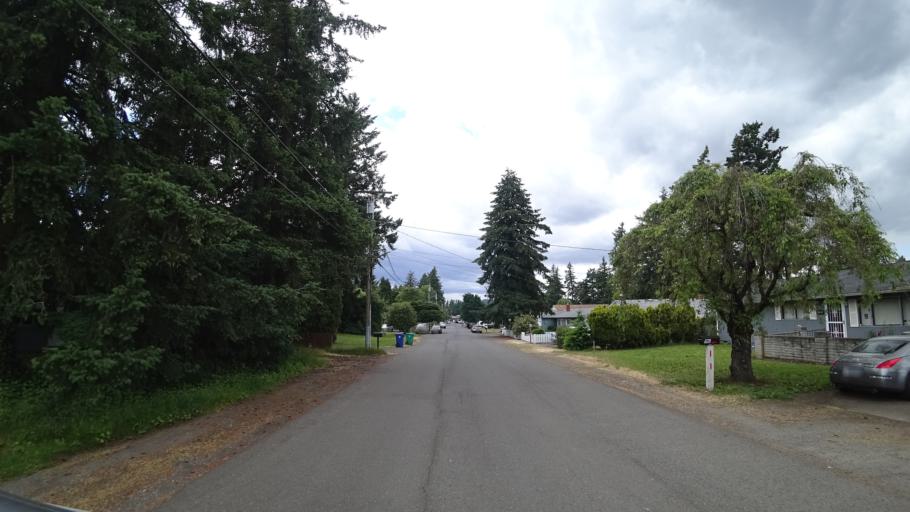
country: US
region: Oregon
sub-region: Multnomah County
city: Lents
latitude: 45.4974
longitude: -122.5194
